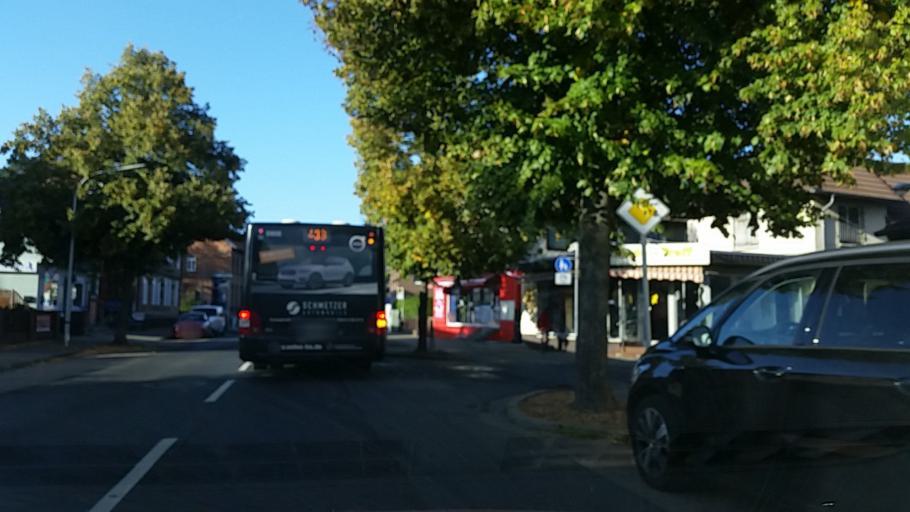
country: DE
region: Lower Saxony
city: Braunschweig
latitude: 52.2918
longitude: 10.5607
